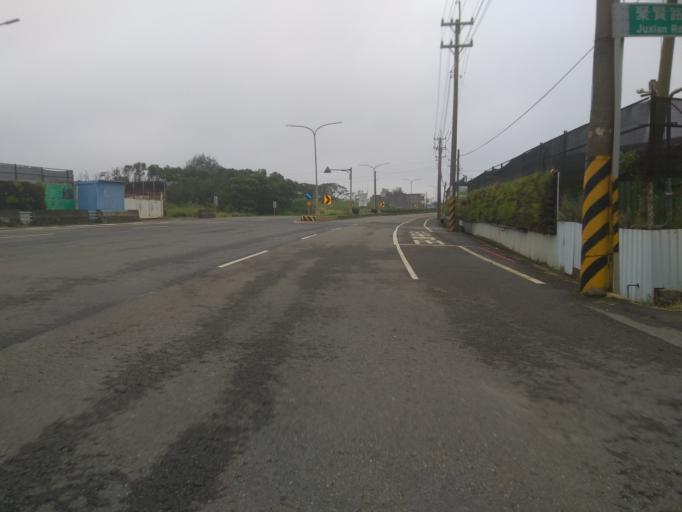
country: TW
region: Taiwan
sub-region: Hsinchu
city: Zhubei
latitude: 24.9946
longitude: 121.0347
